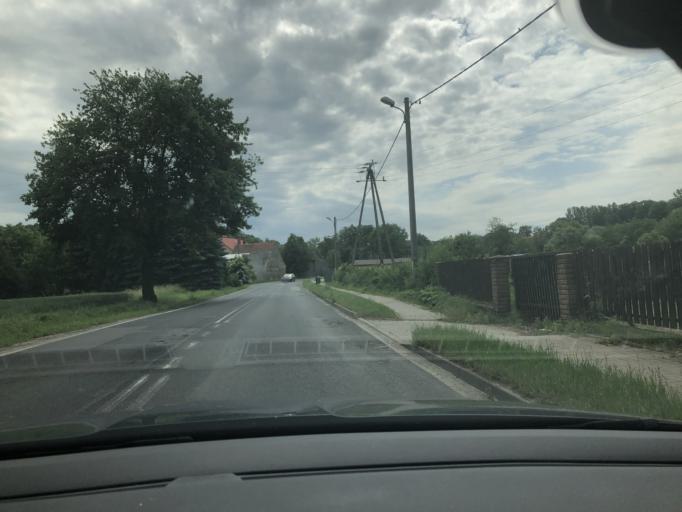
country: PL
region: Lower Silesian Voivodeship
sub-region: Powiat zlotoryjski
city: Zlotoryja
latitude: 51.1351
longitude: 15.9266
